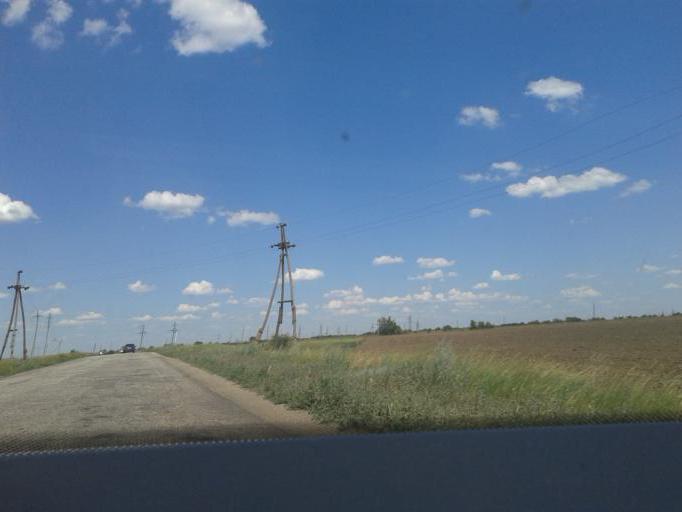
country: RU
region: Volgograd
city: Frolovo
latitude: 49.7039
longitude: 43.6550
